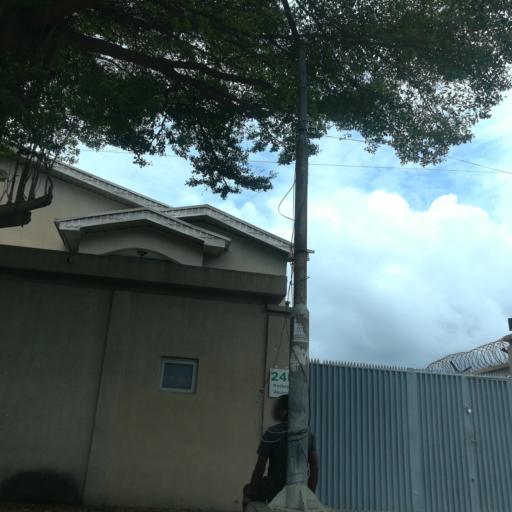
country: NG
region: Lagos
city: Ikoyi
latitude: 6.4431
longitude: 3.4597
